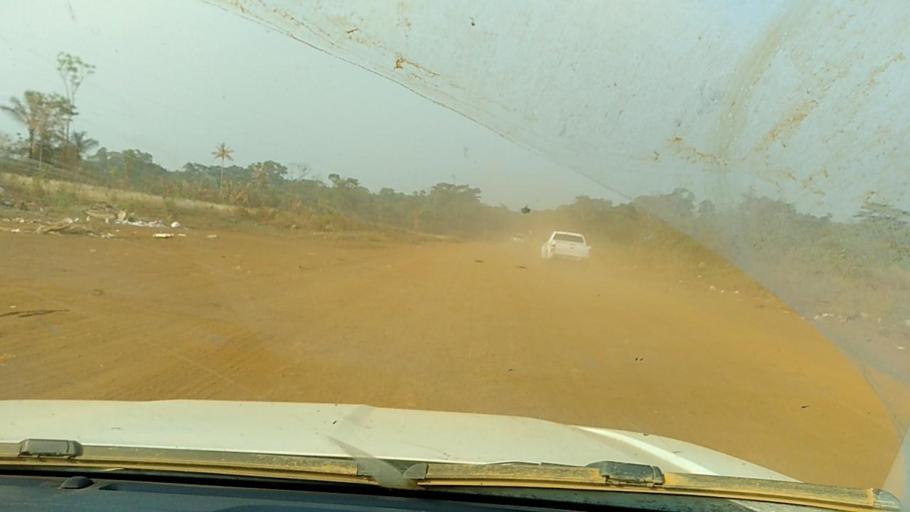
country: BR
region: Rondonia
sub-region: Porto Velho
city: Porto Velho
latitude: -8.7365
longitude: -63.9670
